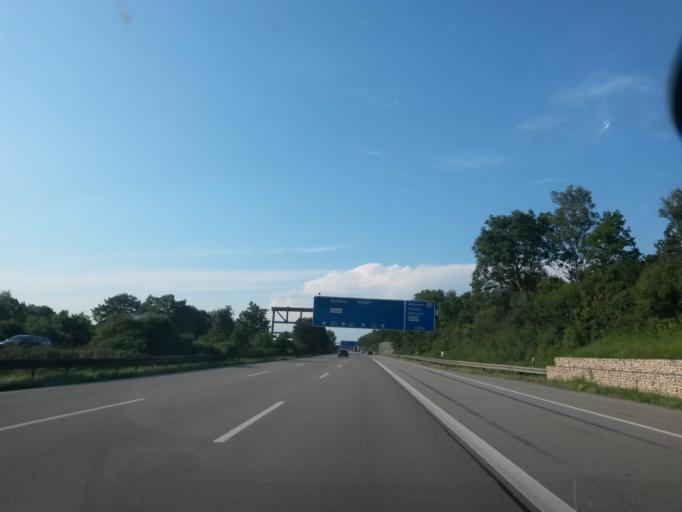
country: DE
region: Bavaria
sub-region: Upper Bavaria
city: Vaterstetten
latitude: 48.1315
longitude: 11.7595
